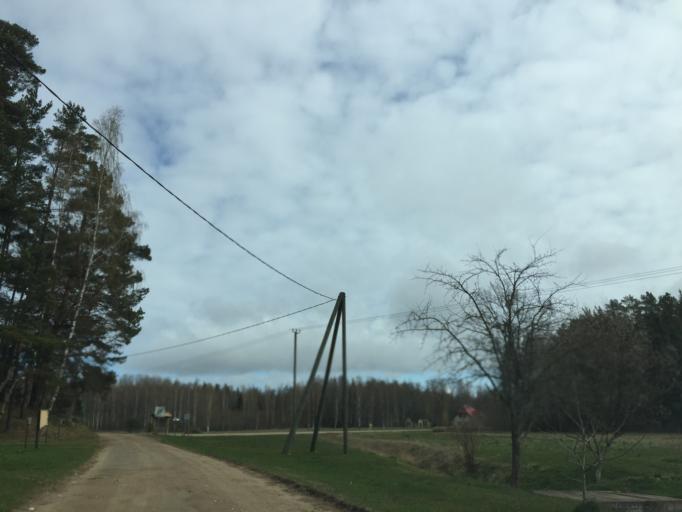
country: LV
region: Salacgrivas
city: Salacgriva
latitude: 57.5325
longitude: 24.3751
